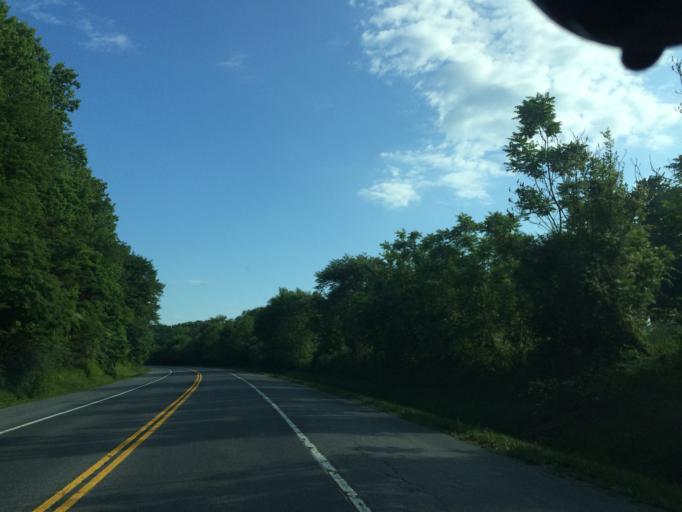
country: US
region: Maryland
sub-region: Carroll County
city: Eldersburg
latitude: 39.4453
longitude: -76.9968
